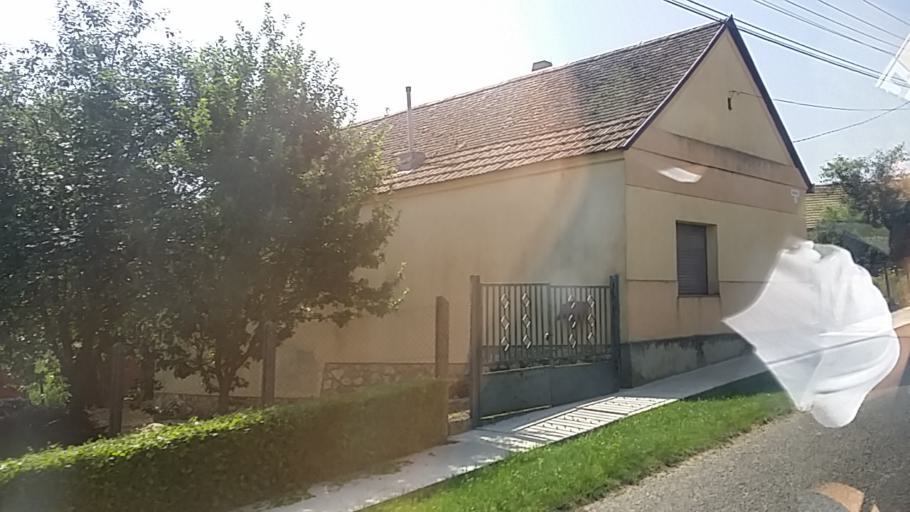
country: HU
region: Baranya
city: Siklos
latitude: 45.9060
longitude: 18.3332
